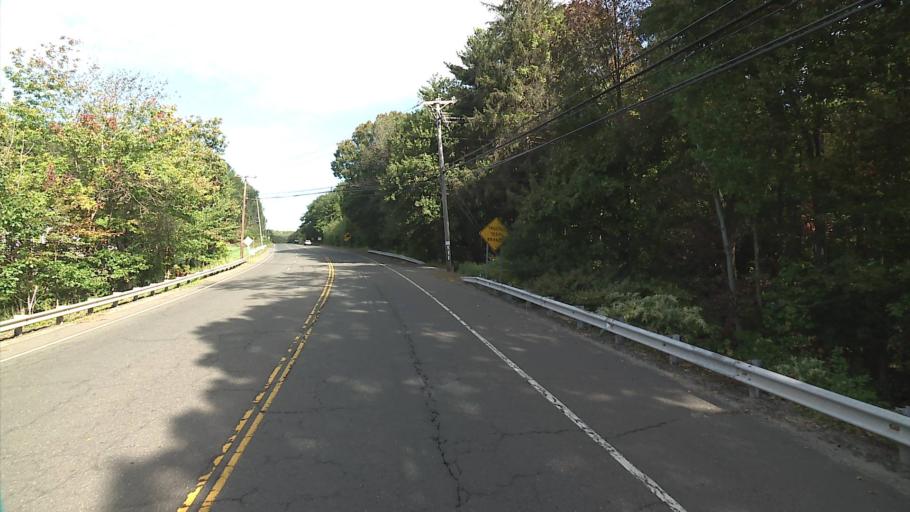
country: US
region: Connecticut
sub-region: Hartford County
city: Bristol
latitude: 41.6488
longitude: -72.9640
